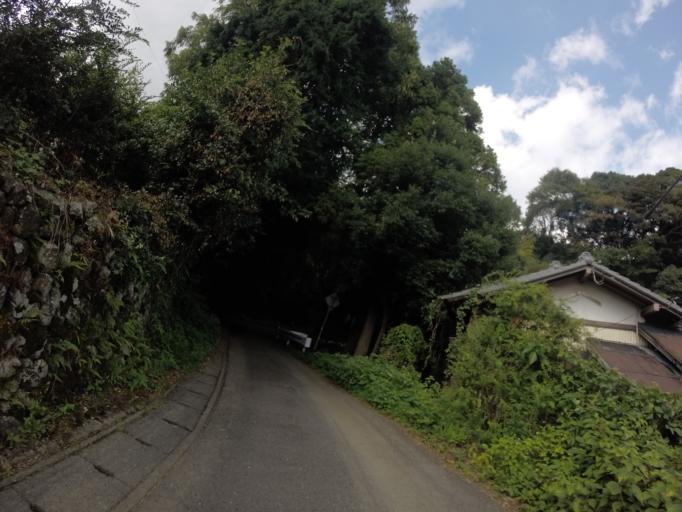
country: JP
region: Shizuoka
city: Shizuoka-shi
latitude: 35.0875
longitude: 138.4607
